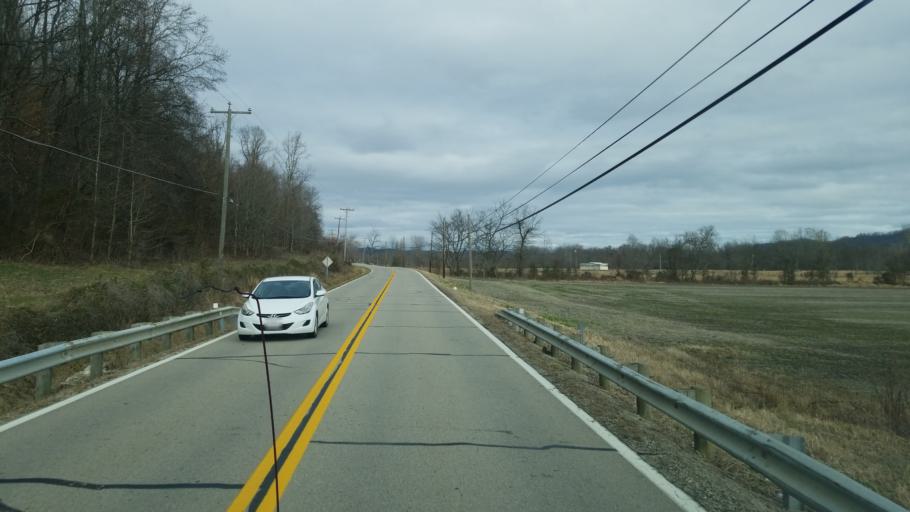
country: US
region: Ohio
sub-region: Scioto County
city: West Portsmouth
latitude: 38.6506
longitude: -83.1348
